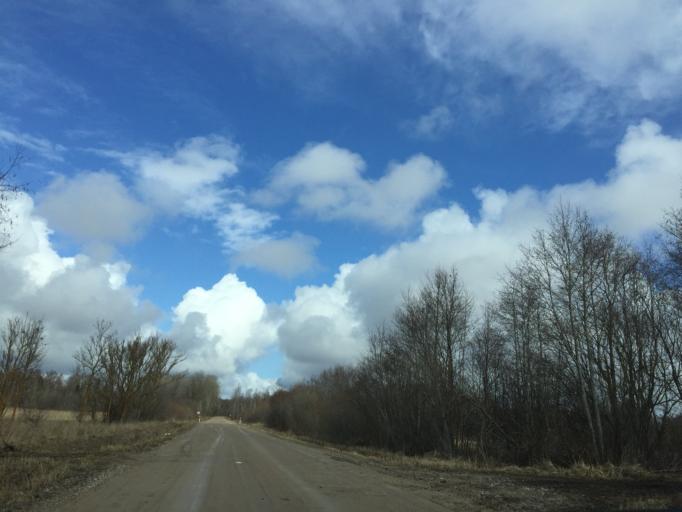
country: EE
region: Laeaene
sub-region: Lihula vald
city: Lihula
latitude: 58.7151
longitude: 23.8209
